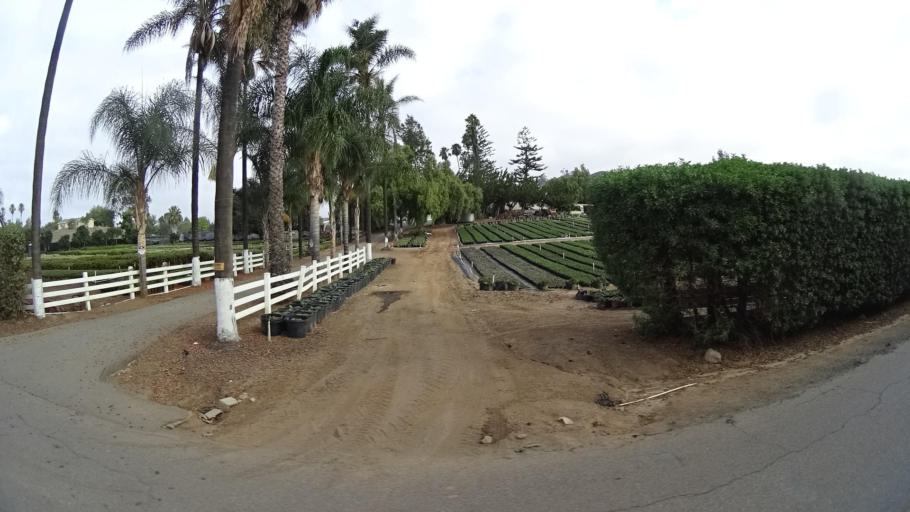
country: US
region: California
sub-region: San Diego County
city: San Marcos
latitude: 33.1793
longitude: -117.1696
